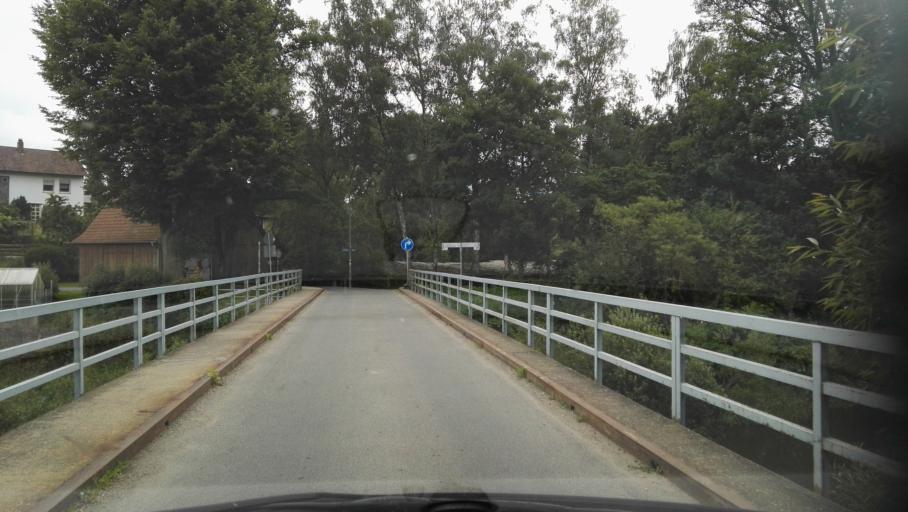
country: DE
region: Bavaria
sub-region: Upper Franconia
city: Redwitz an der Rodach
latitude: 50.1752
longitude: 11.2012
